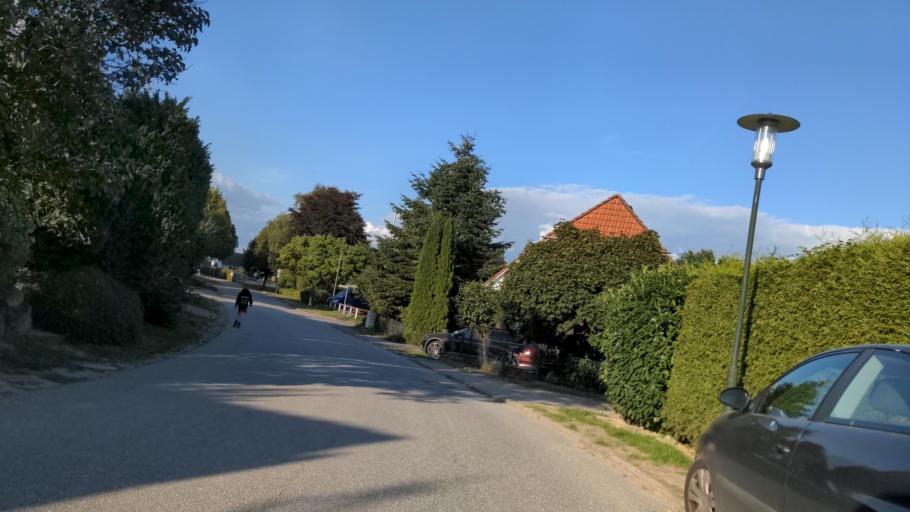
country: DE
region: Schleswig-Holstein
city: Ahrensbok
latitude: 53.9793
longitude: 10.6302
